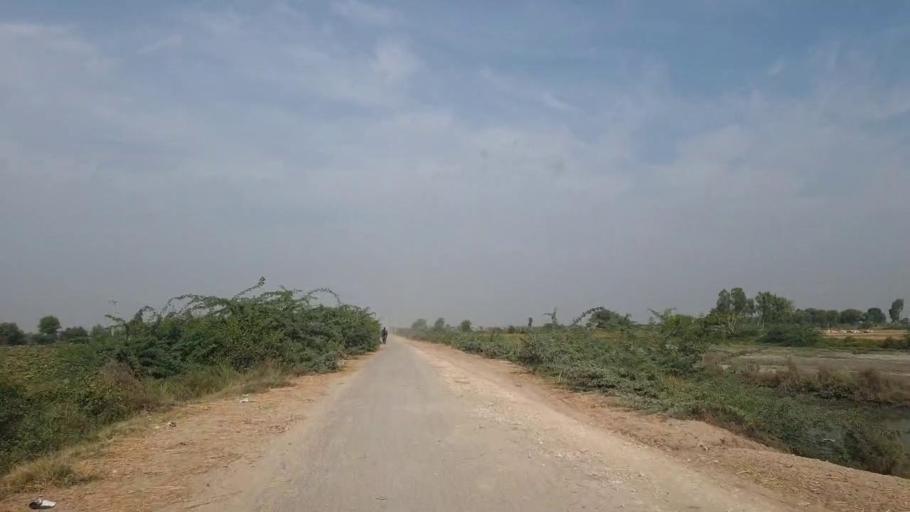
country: PK
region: Sindh
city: Tando Bago
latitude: 24.9012
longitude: 68.9981
